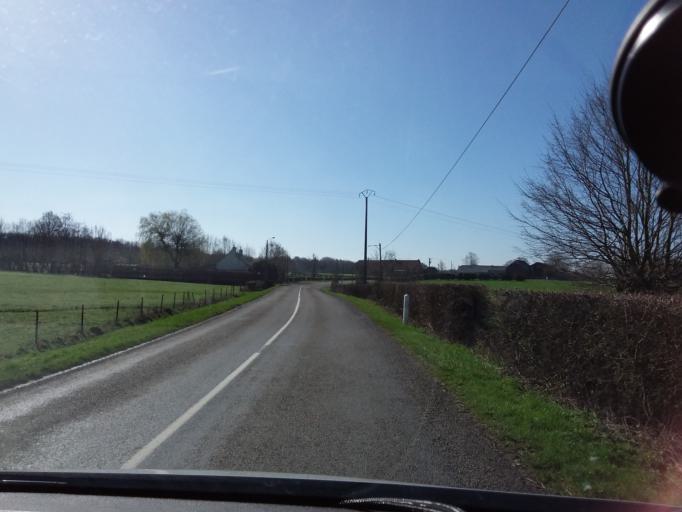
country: FR
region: Nord-Pas-de-Calais
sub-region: Departement du Nord
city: Anor
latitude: 49.9596
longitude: 4.0810
